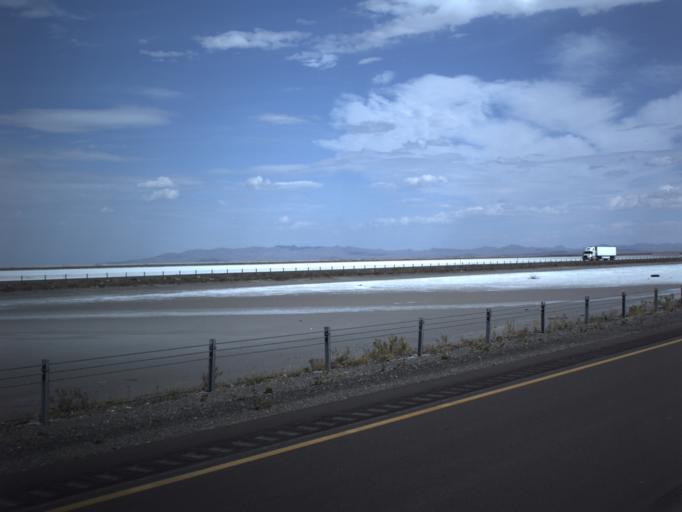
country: US
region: Utah
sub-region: Tooele County
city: Wendover
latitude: 40.7286
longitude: -113.4029
